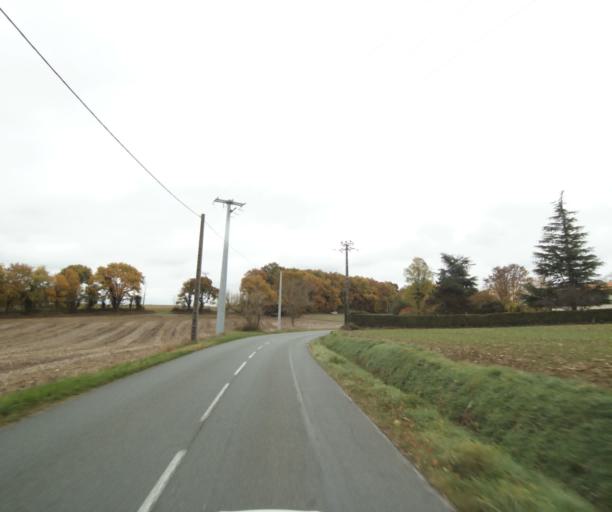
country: FR
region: Poitou-Charentes
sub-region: Departement de la Charente-Maritime
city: Bussac-sur-Charente
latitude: 45.7681
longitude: -0.6457
